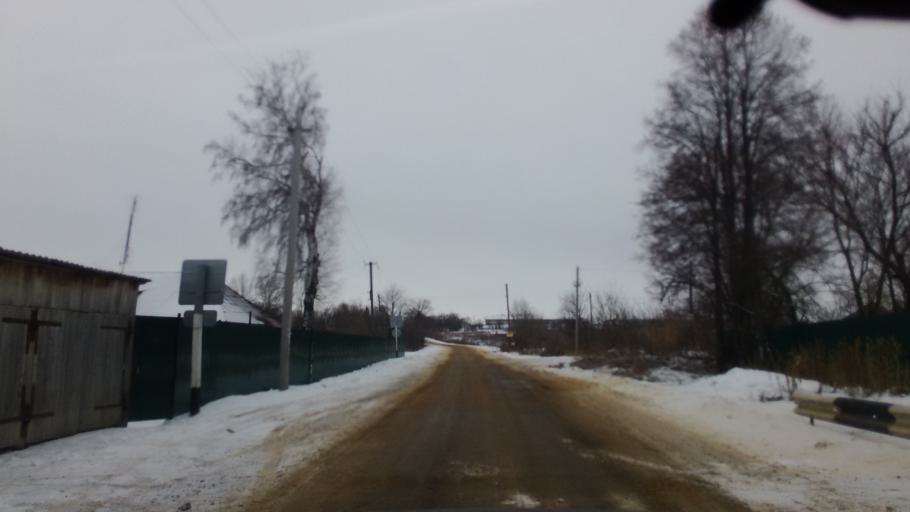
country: RU
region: Tula
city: Bogoroditsk
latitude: 53.7585
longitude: 37.9904
